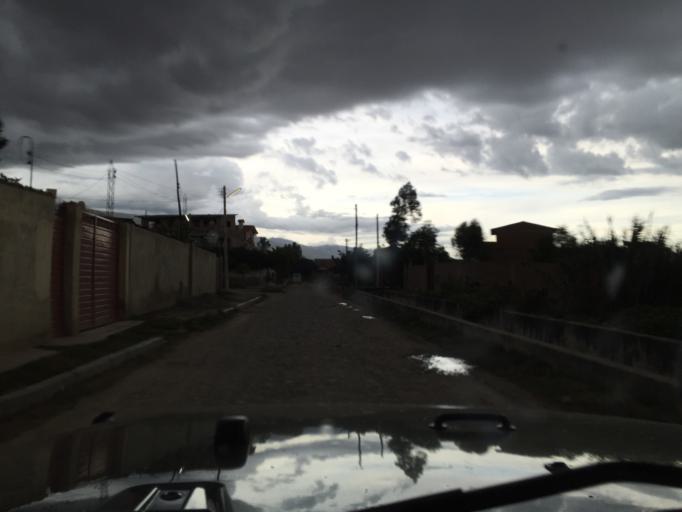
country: BO
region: Cochabamba
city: Cochabamba
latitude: -17.3966
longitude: -66.2122
